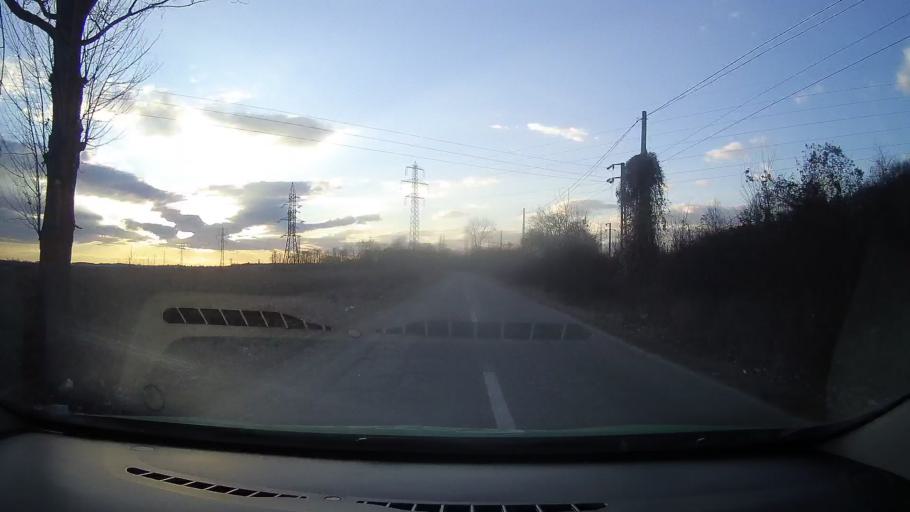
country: RO
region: Dambovita
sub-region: Comuna Gura Ocnitei
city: Gura Ocnitei
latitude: 44.9361
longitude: 25.5884
